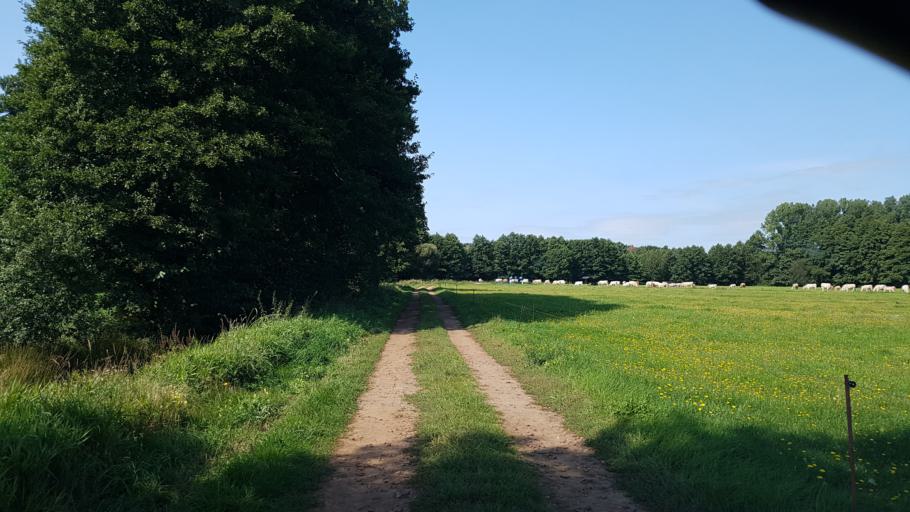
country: DE
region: Brandenburg
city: Schonewalde
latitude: 51.6621
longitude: 13.6231
